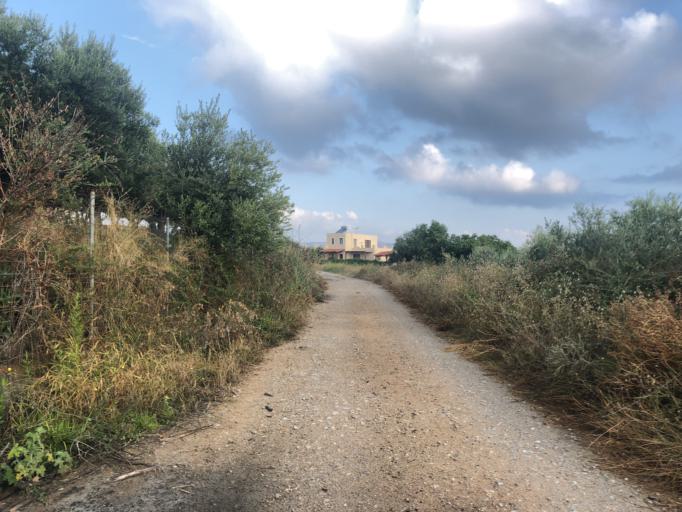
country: GR
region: Crete
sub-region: Nomos Chanias
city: Georgioupolis
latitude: 35.3472
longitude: 24.3112
